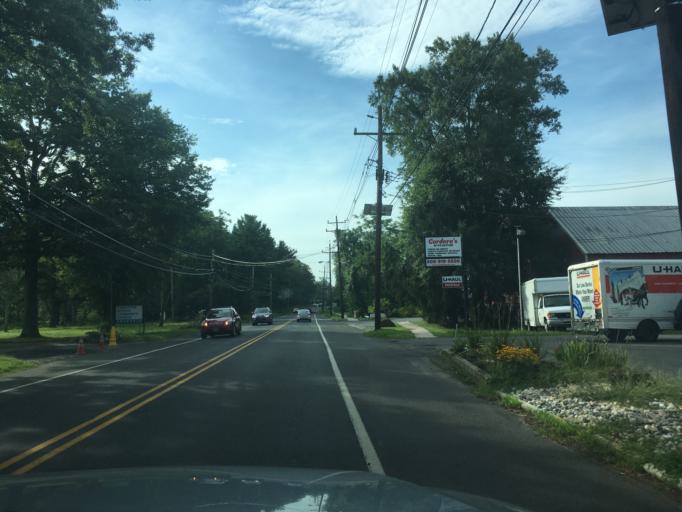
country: US
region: New Jersey
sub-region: Mercer County
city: Princeton Junction
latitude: 40.3232
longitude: -74.6274
